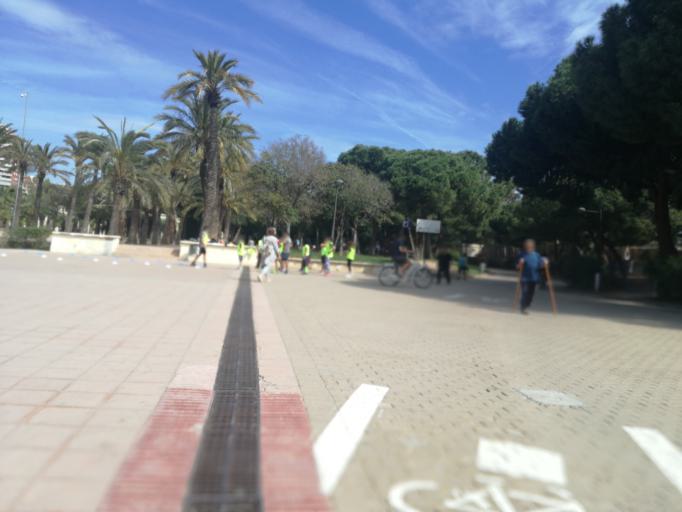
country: ES
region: Valencia
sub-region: Provincia de Valencia
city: Valencia
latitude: 39.4664
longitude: -0.3612
